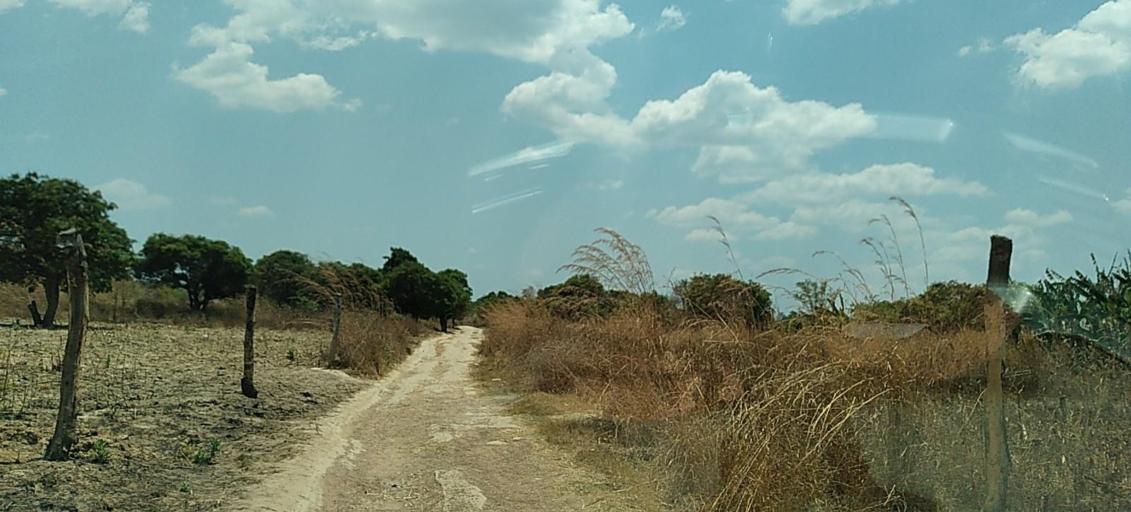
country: ZM
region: Copperbelt
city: Chililabombwe
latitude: -12.4864
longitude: 27.6680
